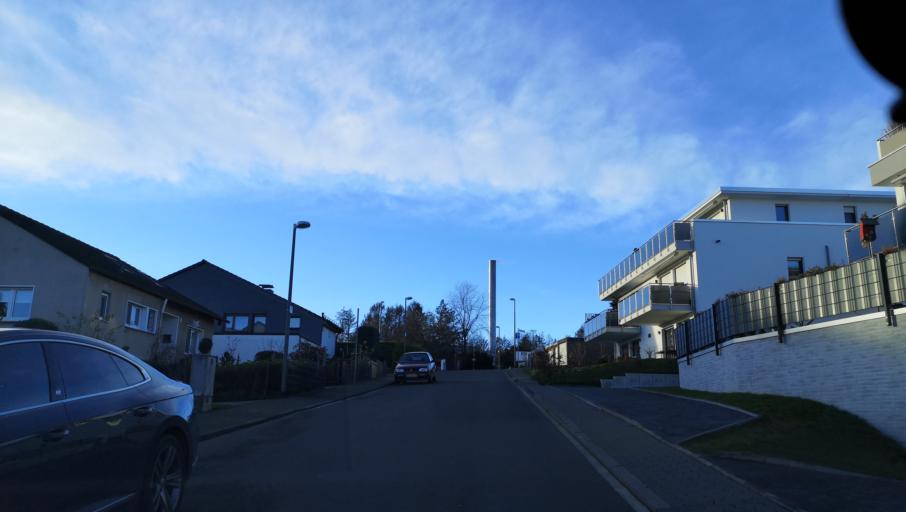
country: DE
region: North Rhine-Westphalia
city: Radevormwald
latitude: 51.2094
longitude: 7.3568
